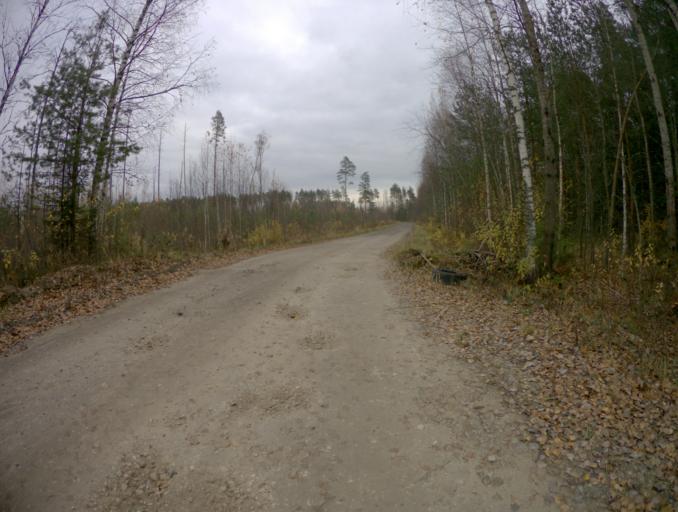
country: RU
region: Moskovskaya
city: Malaya Dubna
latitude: 55.9253
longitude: 38.9896
